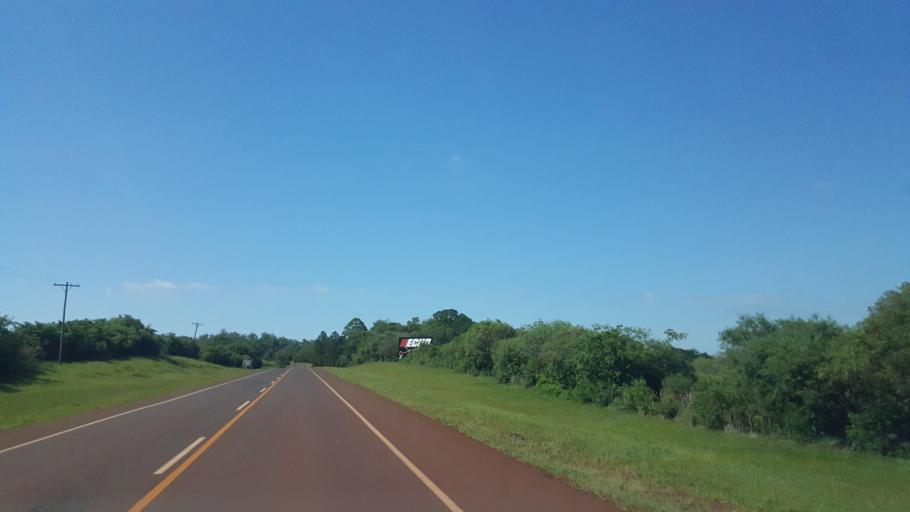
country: AR
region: Misiones
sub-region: Departamento de Apostoles
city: Apostoles
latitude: -27.8675
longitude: -55.7654
